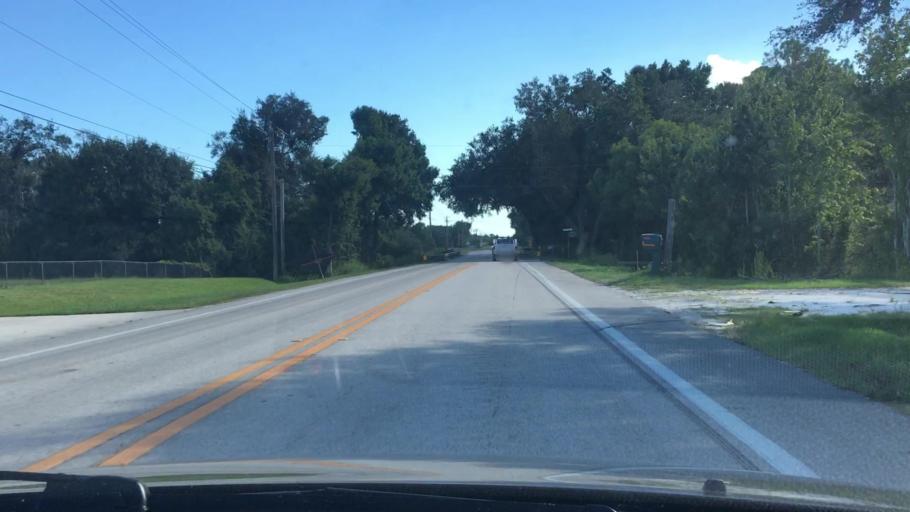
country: US
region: Florida
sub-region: Volusia County
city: Samsula-Spruce Creek
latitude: 29.0886
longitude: -81.0686
